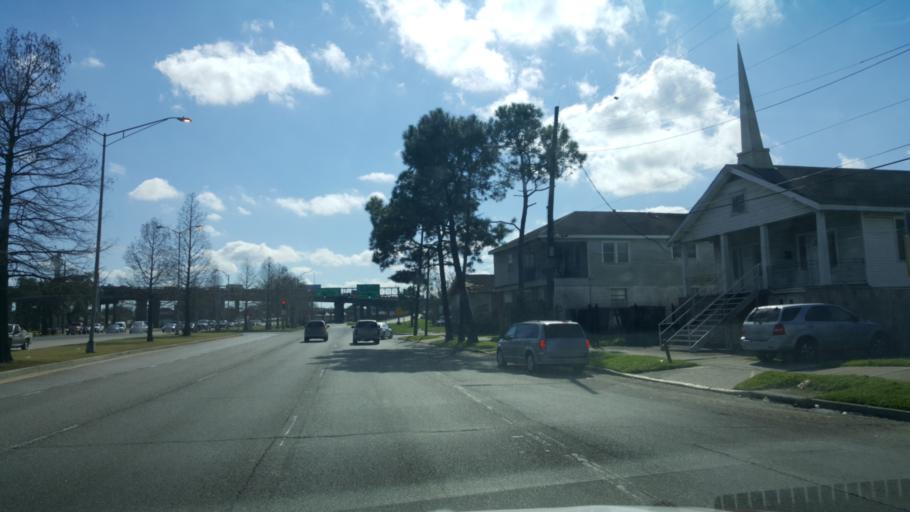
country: US
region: Louisiana
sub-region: Orleans Parish
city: New Orleans
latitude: 29.9836
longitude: -90.0581
